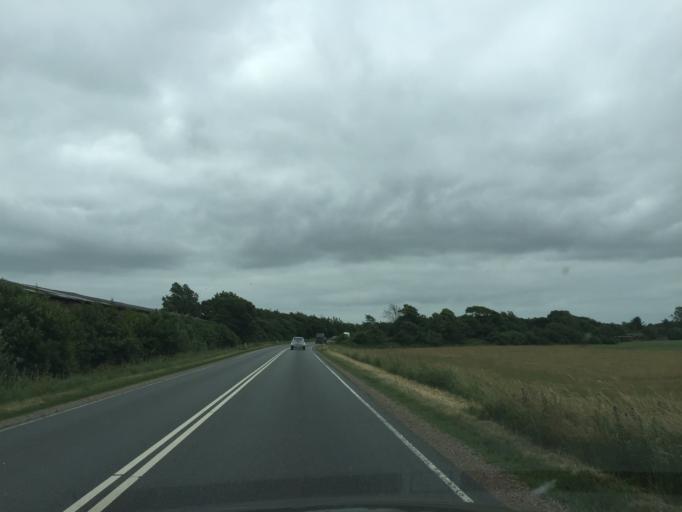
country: DK
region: South Denmark
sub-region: Esbjerg Kommune
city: Ribe
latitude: 55.3254
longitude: 8.7542
